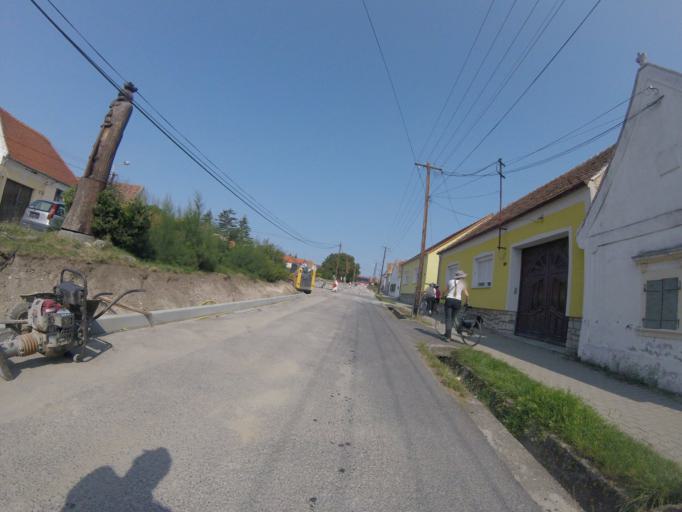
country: HU
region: Gyor-Moson-Sopron
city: Fertorakos
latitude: 47.7203
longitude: 16.6505
